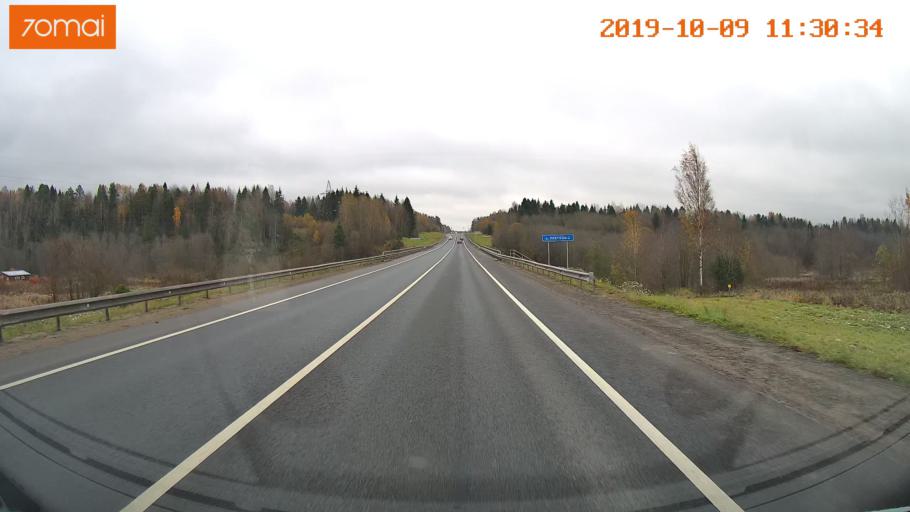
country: RU
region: Vologda
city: Gryazovets
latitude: 59.0527
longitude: 40.0780
